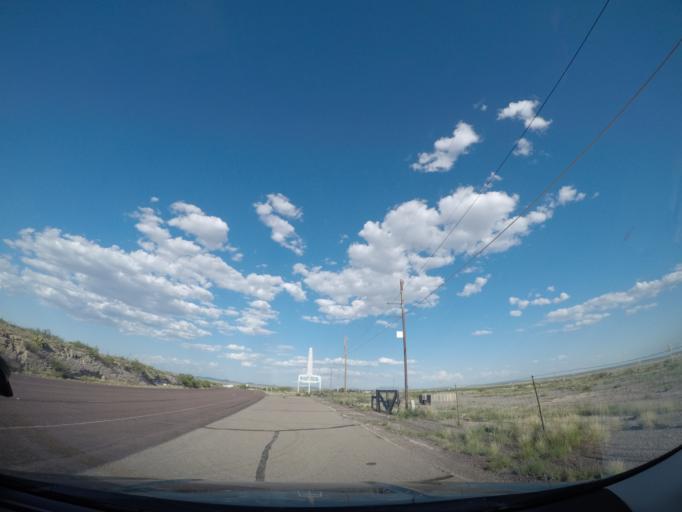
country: US
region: Texas
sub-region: Presidio County
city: Marfa
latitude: 30.3053
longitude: -104.0449
